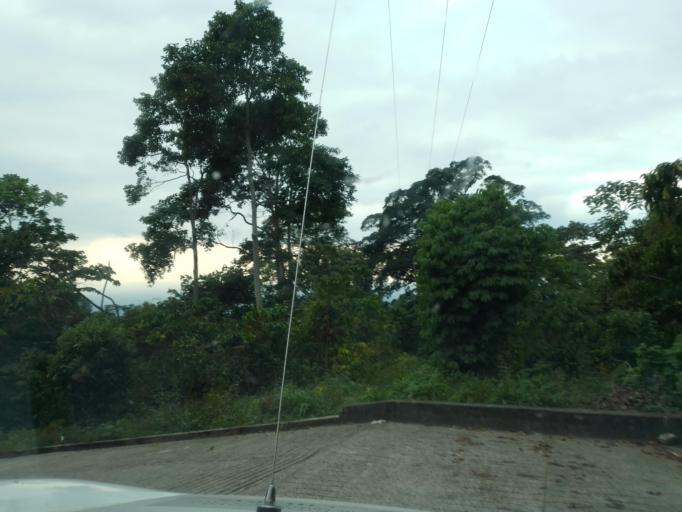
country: MX
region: Chiapas
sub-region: Union Juarez
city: Santo Domingo
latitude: 15.0516
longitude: -92.1162
